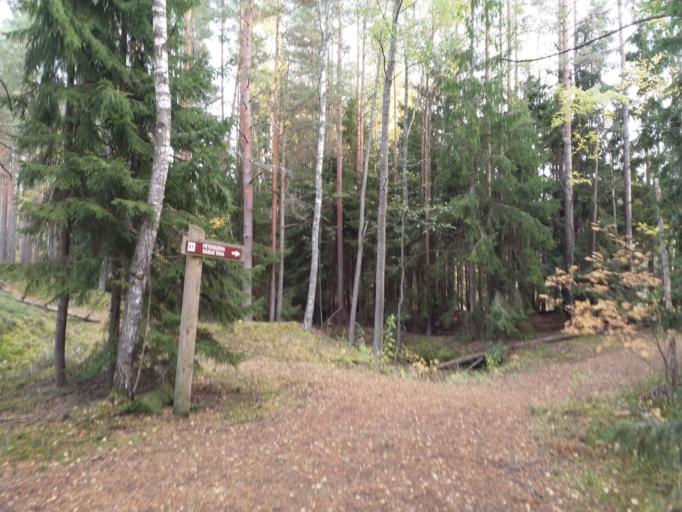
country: LV
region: Dundaga
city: Dundaga
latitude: 57.6553
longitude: 22.2694
